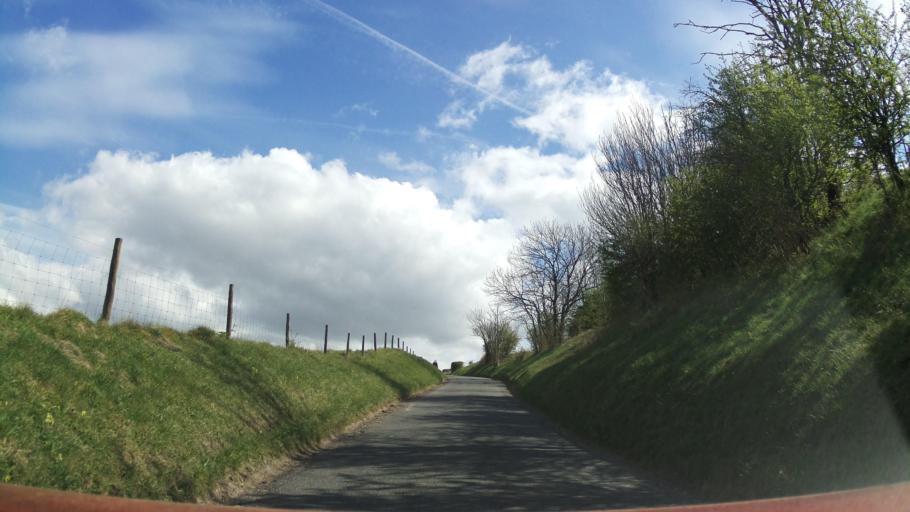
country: GB
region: England
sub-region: West Berkshire
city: Kintbury
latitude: 51.3581
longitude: -1.4730
